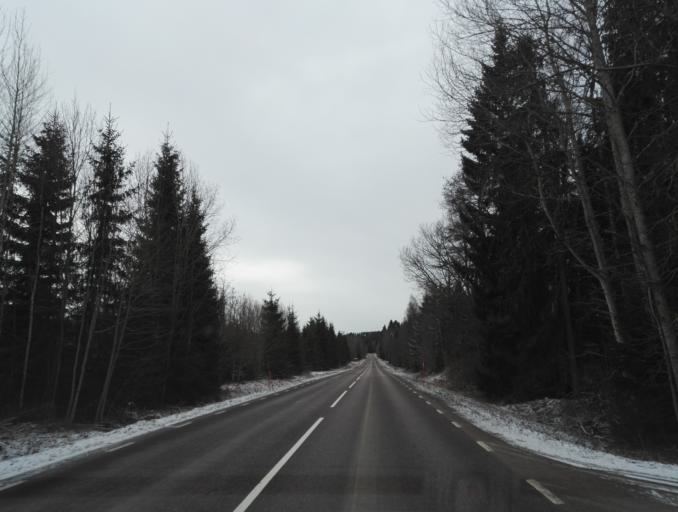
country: SE
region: Kalmar
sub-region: Hultsfreds Kommun
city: Virserum
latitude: 57.3862
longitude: 15.6066
